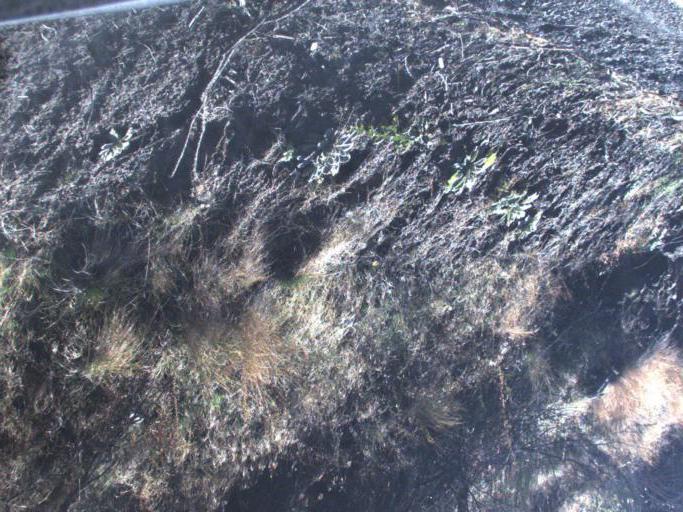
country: US
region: Washington
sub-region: Asotin County
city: Asotin
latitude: 46.0484
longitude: -117.2426
